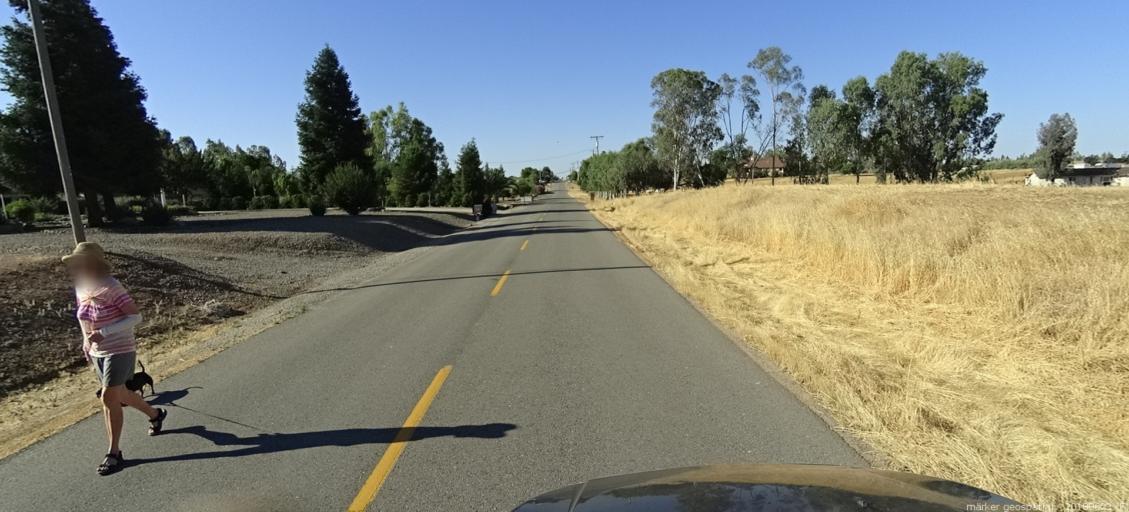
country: US
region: California
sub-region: Madera County
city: Bonadelle Ranchos-Madera Ranchos
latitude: 36.9636
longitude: -119.7984
